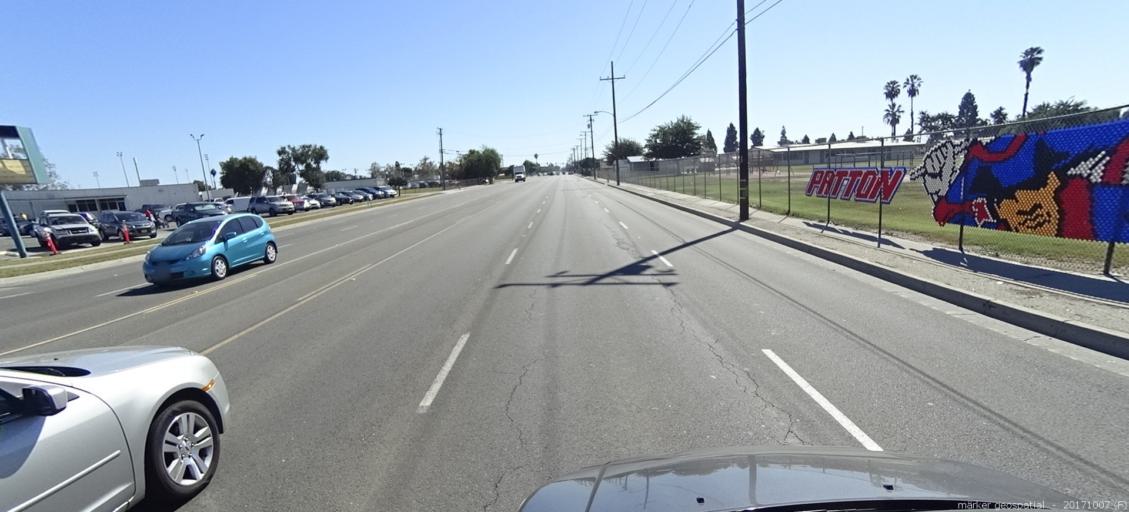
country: US
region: California
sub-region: Orange County
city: Stanton
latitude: 33.7914
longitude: -118.0112
